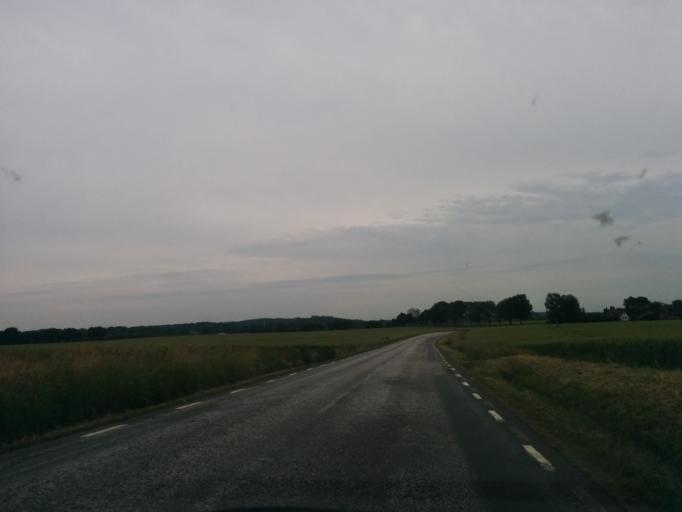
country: SE
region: Skane
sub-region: Lunds Kommun
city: Genarp
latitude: 55.6278
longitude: 13.3838
